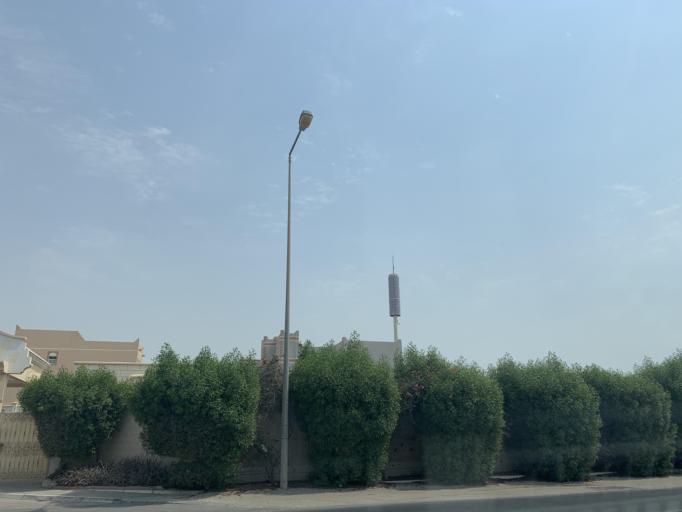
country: BH
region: Manama
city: Jidd Hafs
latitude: 26.2132
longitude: 50.4841
